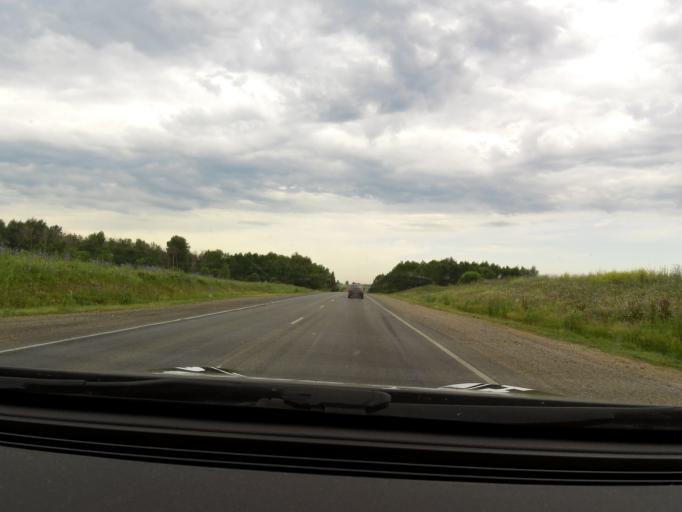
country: RU
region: Bashkortostan
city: Kudeyevskiy
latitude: 54.8171
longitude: 56.7846
